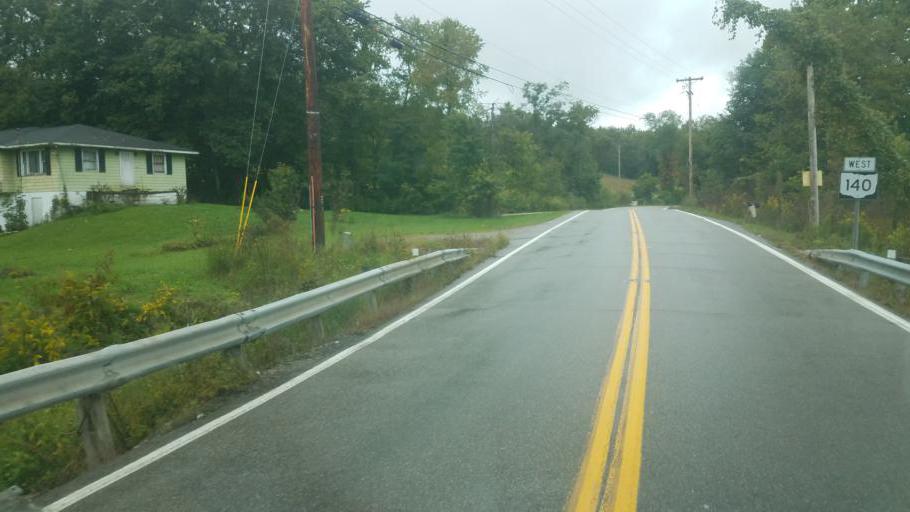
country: US
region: Ohio
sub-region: Jackson County
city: Oak Hill
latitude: 38.8597
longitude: -82.6009
